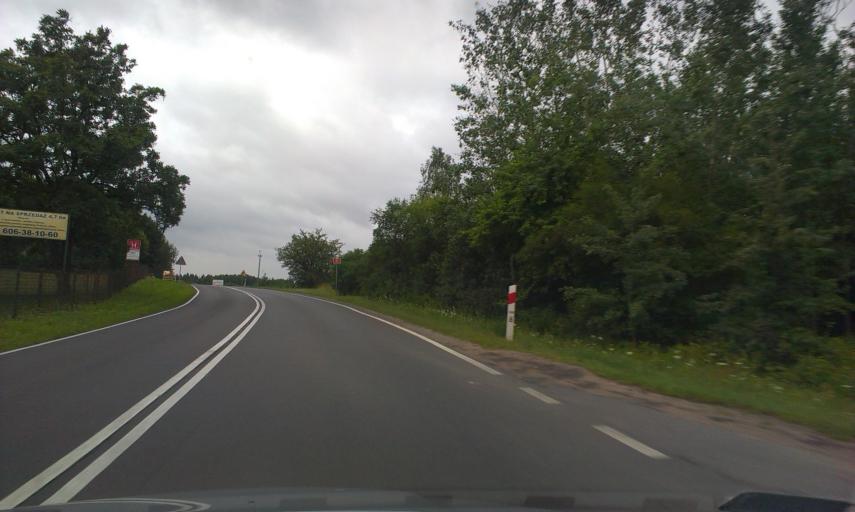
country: PL
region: Greater Poland Voivodeship
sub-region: Powiat pilski
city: Pila
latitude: 53.2188
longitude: 16.7862
